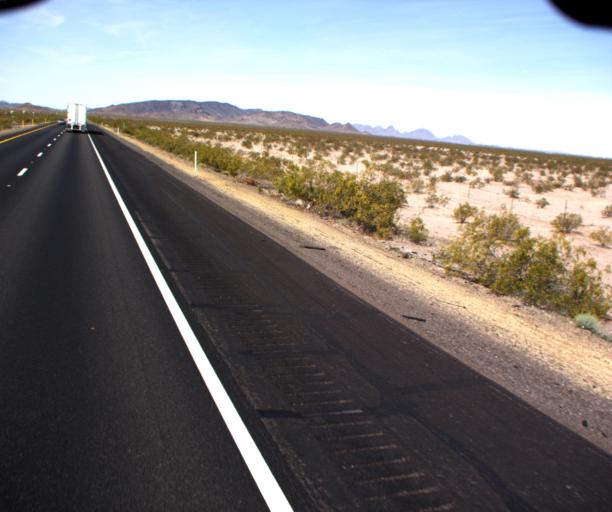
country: US
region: Arizona
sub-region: La Paz County
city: Salome
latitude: 33.6394
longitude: -113.8233
